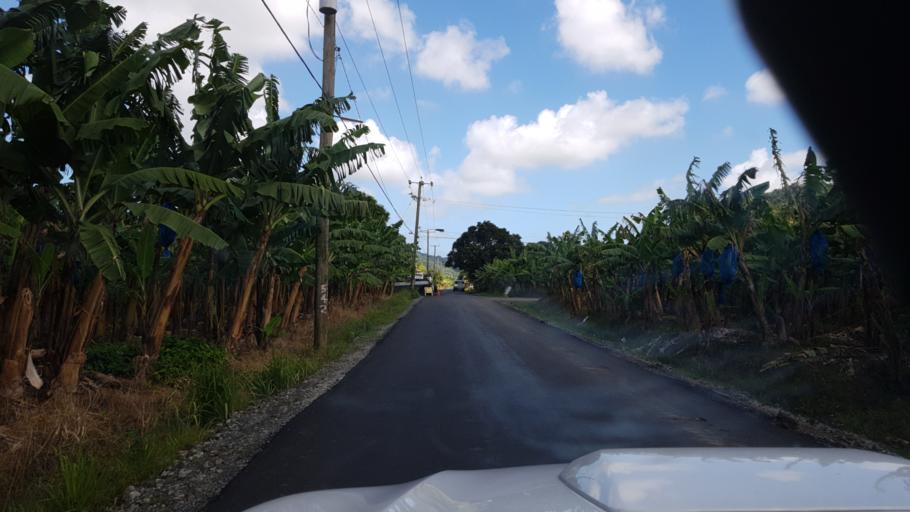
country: LC
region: Anse-la-Raye
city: Anse La Raye
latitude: 13.9537
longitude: -61.0179
